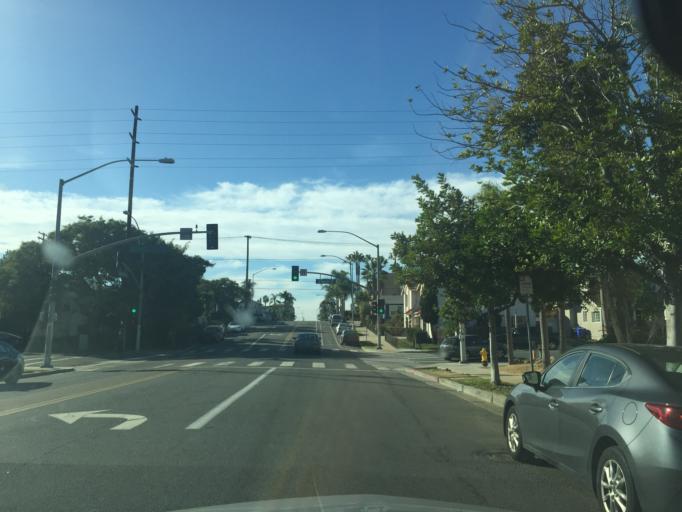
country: US
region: California
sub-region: San Diego County
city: San Diego
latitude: 32.7504
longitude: -117.1247
